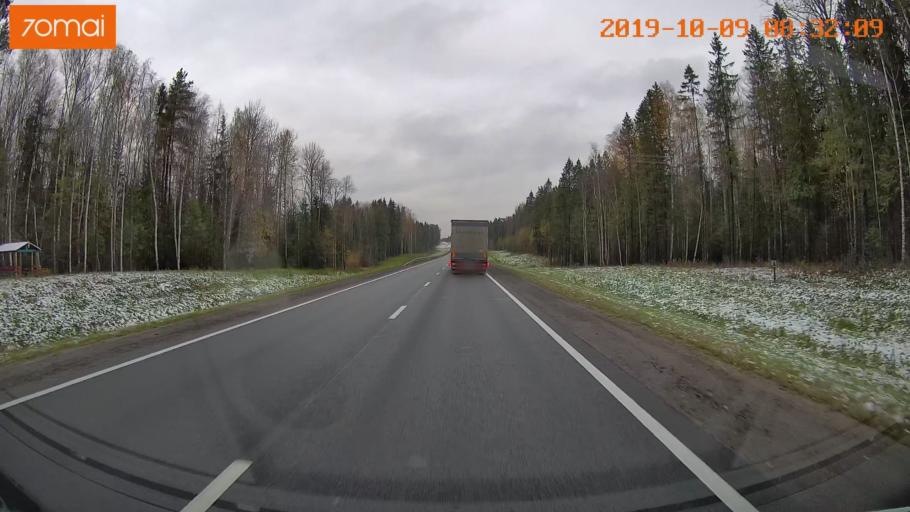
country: RU
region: Vologda
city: Gryazovets
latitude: 58.8628
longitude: 40.1985
